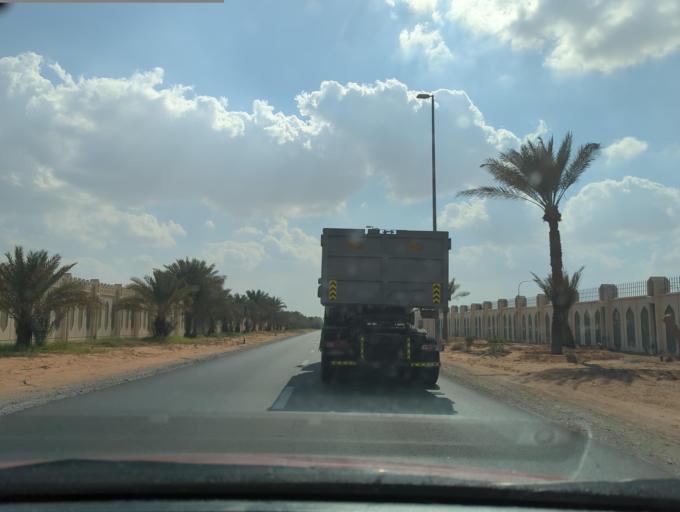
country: AE
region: Abu Dhabi
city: Al Ain
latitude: 24.1737
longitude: 55.6504
